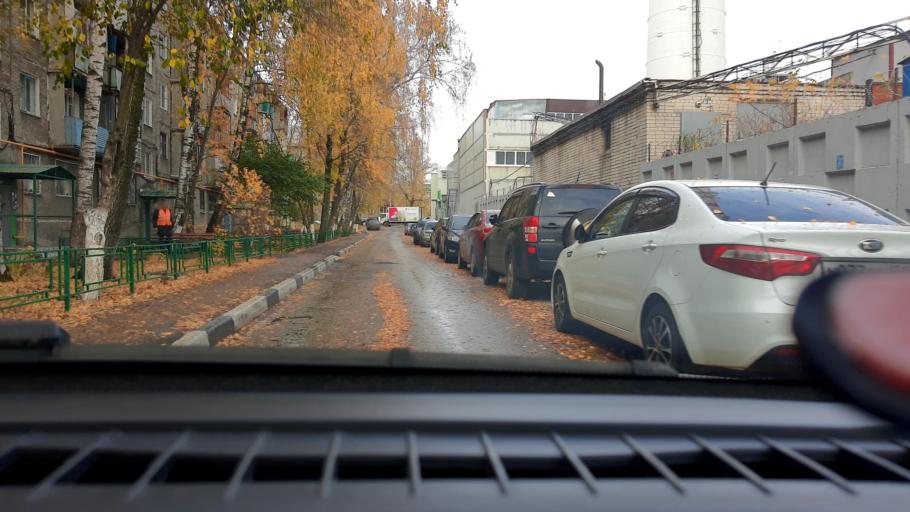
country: RU
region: Nizjnij Novgorod
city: Nizhniy Novgorod
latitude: 56.2881
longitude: 43.9368
